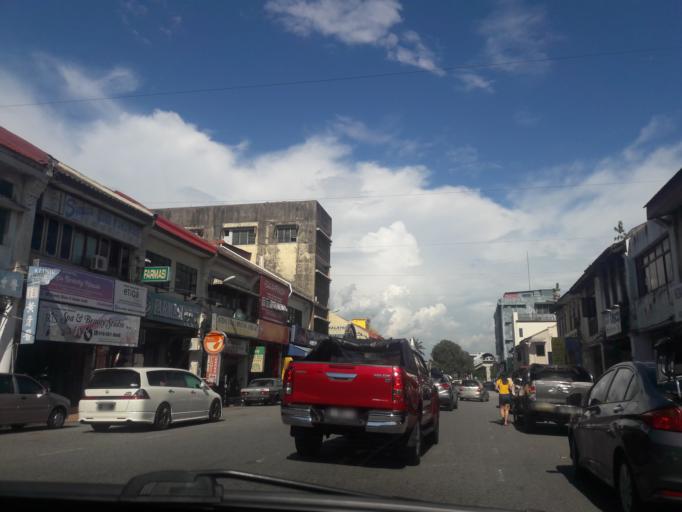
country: MY
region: Kedah
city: Sungai Petani
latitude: 5.6415
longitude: 100.4874
